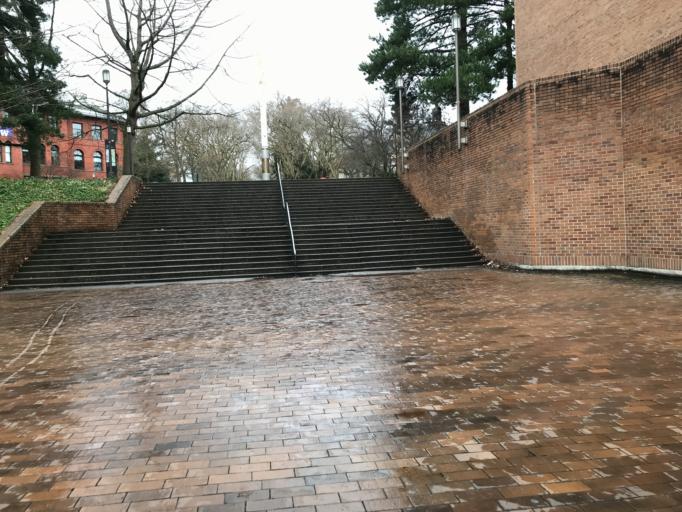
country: US
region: Washington
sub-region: King County
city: Seattle
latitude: 47.6566
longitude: -122.3098
